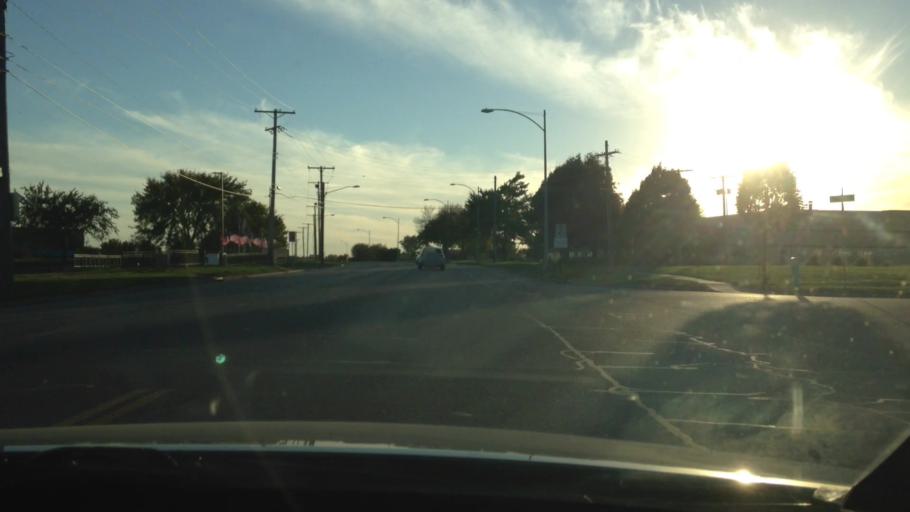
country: US
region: Kansas
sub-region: Johnson County
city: Olathe
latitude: 38.9060
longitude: -94.7821
